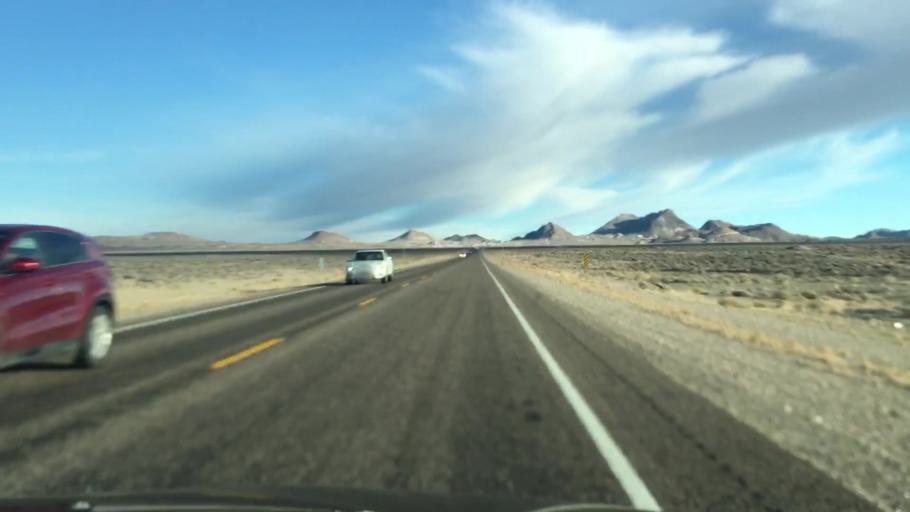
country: US
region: Nevada
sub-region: Nye County
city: Tonopah
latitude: 38.0985
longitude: -117.3236
